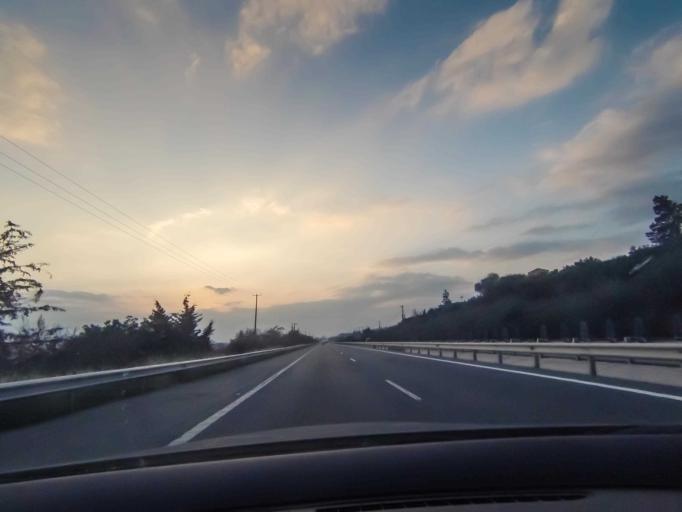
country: CY
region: Limassol
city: Mouttagiaka
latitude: 34.7094
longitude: 33.1177
